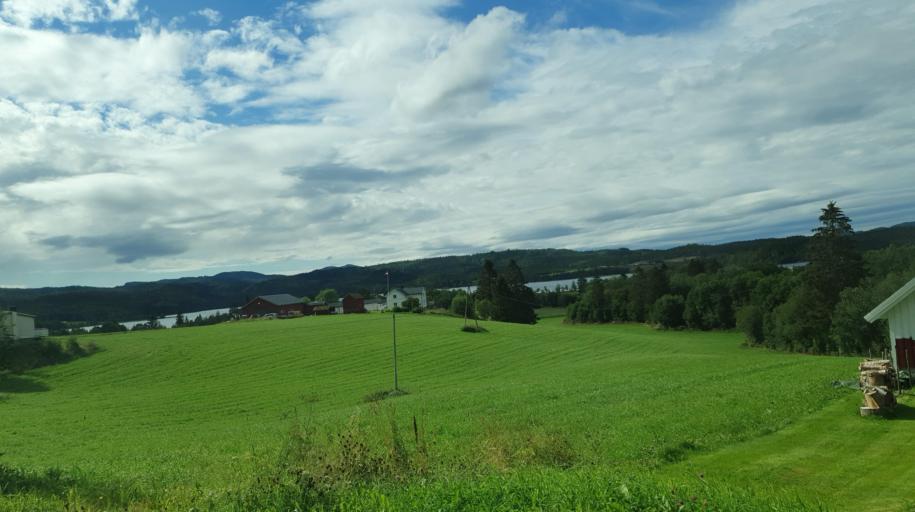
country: NO
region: Nord-Trondelag
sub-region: Levanger
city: Skogn
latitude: 63.6131
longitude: 11.2805
